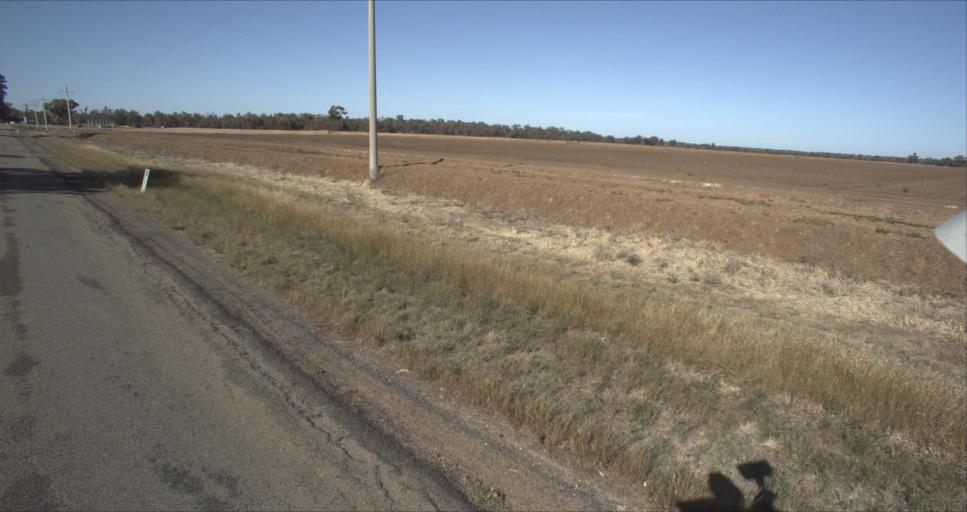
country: AU
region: New South Wales
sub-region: Leeton
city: Leeton
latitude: -34.6023
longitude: 146.2574
